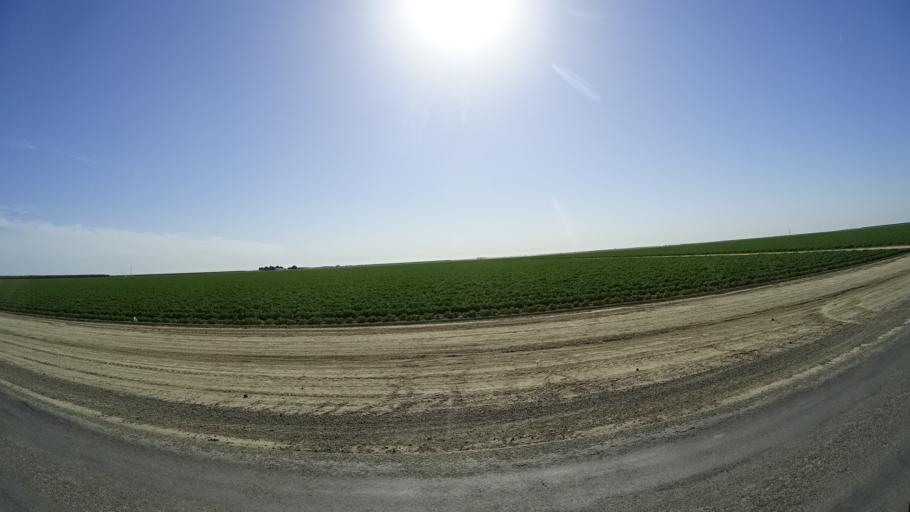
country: US
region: California
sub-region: Fresno County
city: Huron
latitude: 36.1311
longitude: -120.0037
